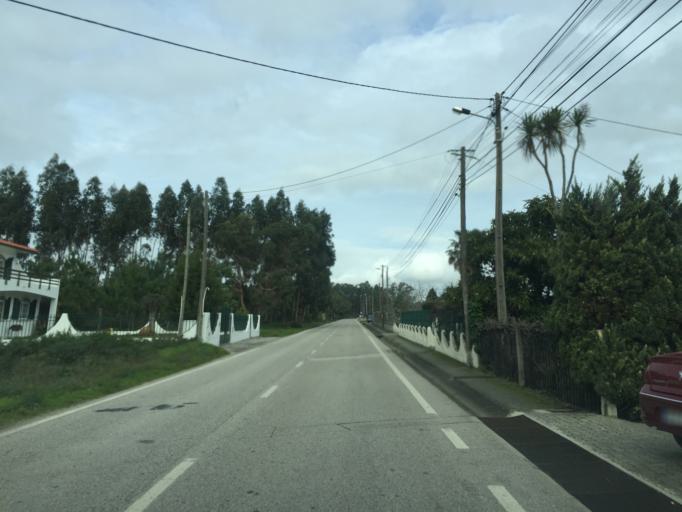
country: PT
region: Coimbra
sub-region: Figueira da Foz
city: Lavos
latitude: 40.0419
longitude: -8.8187
